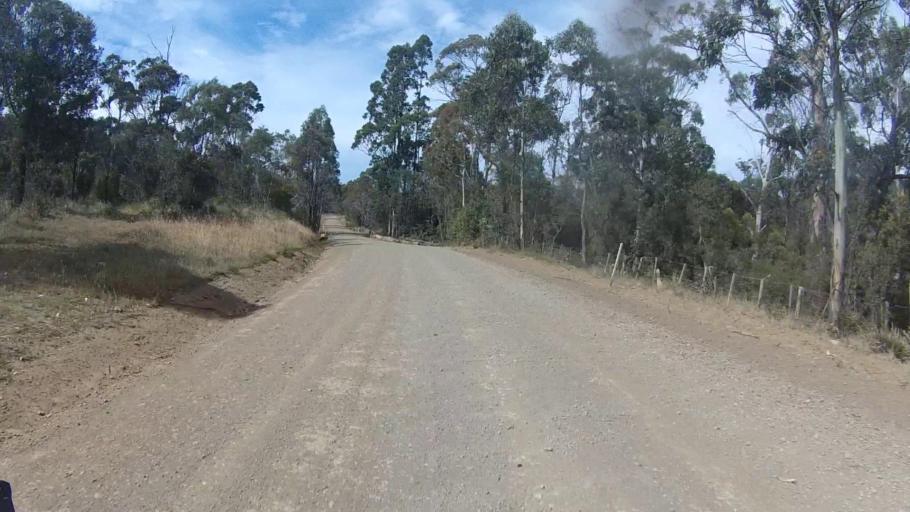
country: AU
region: Tasmania
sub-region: Sorell
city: Sorell
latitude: -42.6500
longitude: 147.8982
